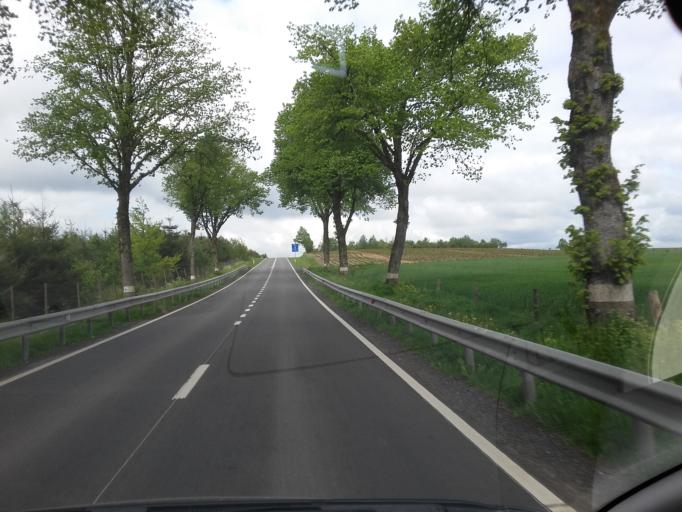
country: BE
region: Wallonia
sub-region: Province du Luxembourg
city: Neufchateau
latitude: 49.8420
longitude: 5.4018
